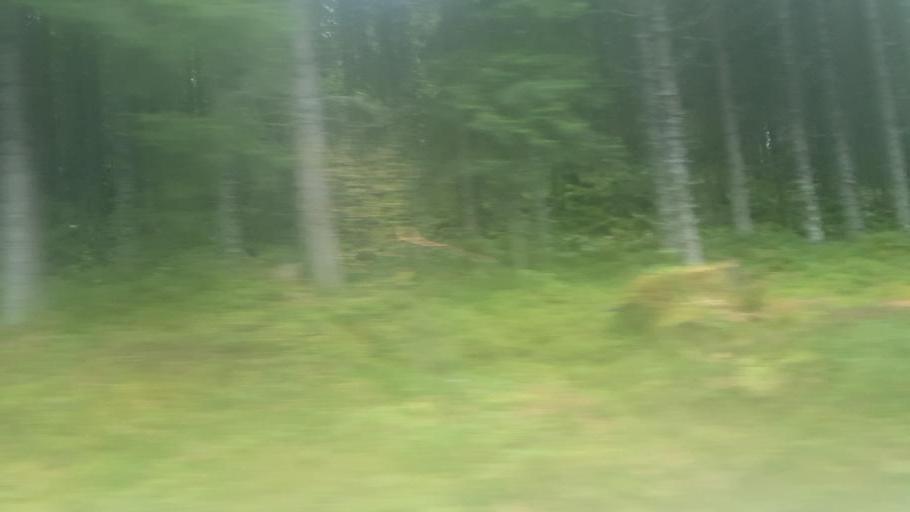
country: NO
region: Nord-Trondelag
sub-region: Levanger
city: Skogn
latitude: 63.6199
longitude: 11.2160
